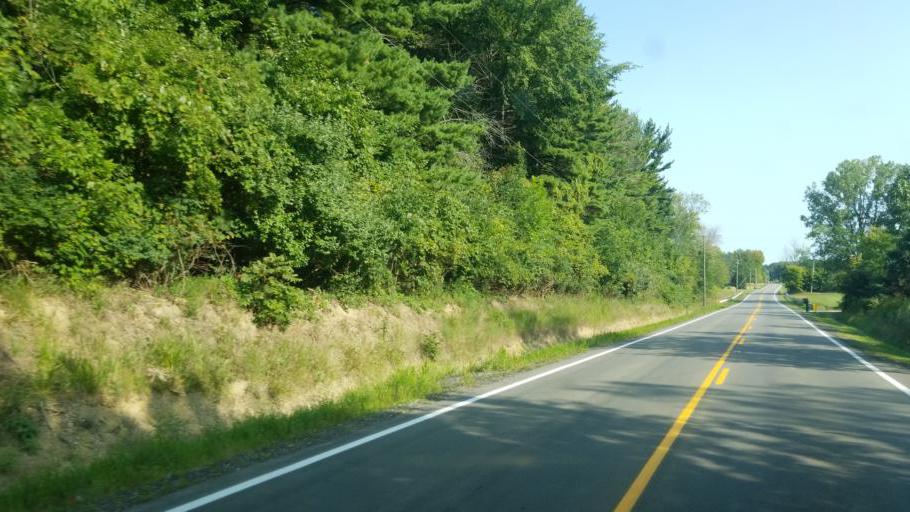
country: US
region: Ohio
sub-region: Richland County
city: Ontario
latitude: 40.7888
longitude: -82.6543
